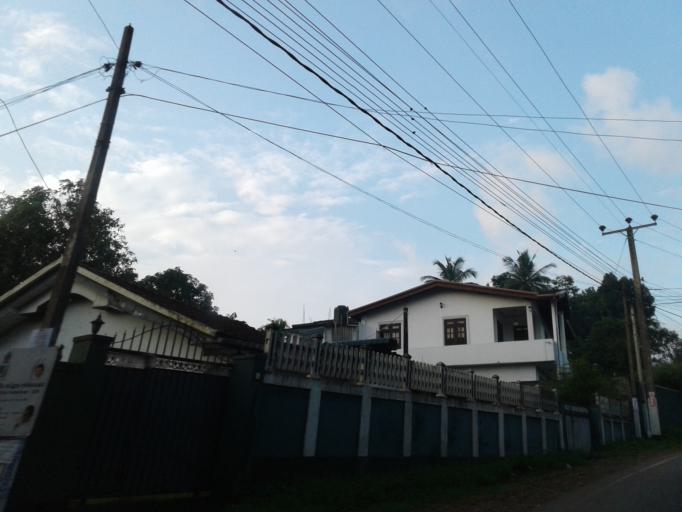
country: LK
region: Western
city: Mulleriyawa
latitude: 6.9661
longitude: 79.9986
